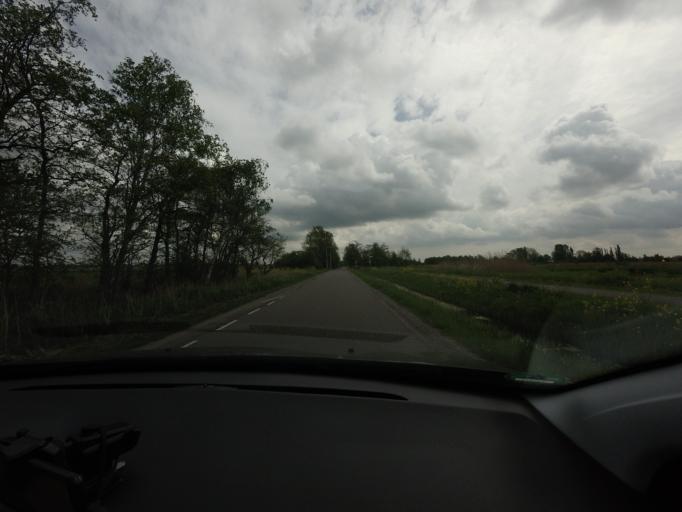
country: NL
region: North Holland
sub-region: Gemeente Landsmeer
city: Landsmeer
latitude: 52.4716
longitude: 4.9075
